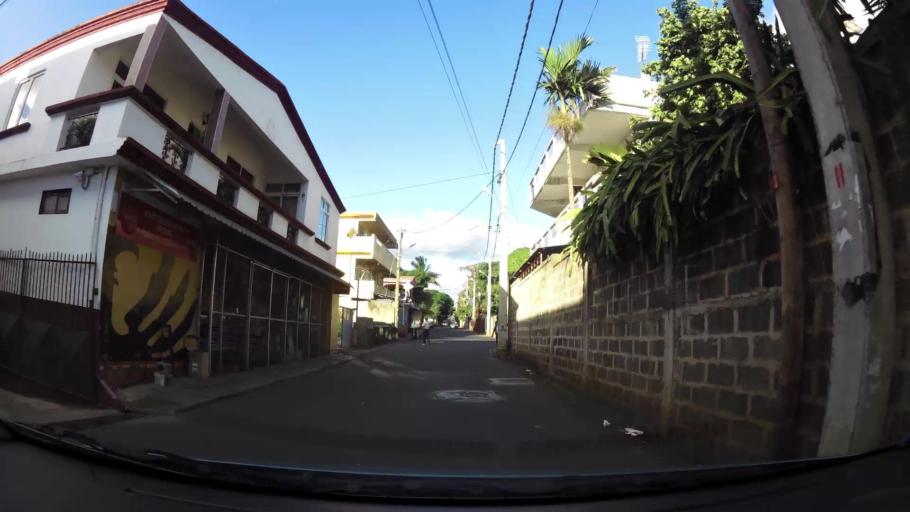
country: MU
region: Black River
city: Petite Riviere
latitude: -20.2190
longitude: 57.4639
